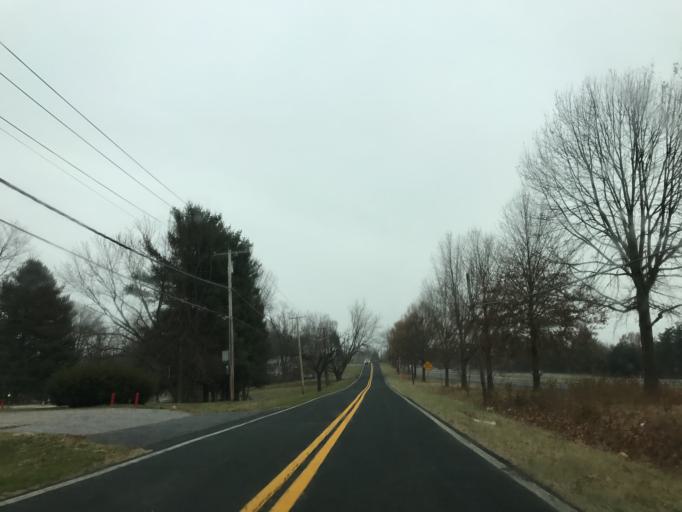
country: US
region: Maryland
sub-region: Baltimore County
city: Reisterstown
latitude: 39.5065
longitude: -76.9020
